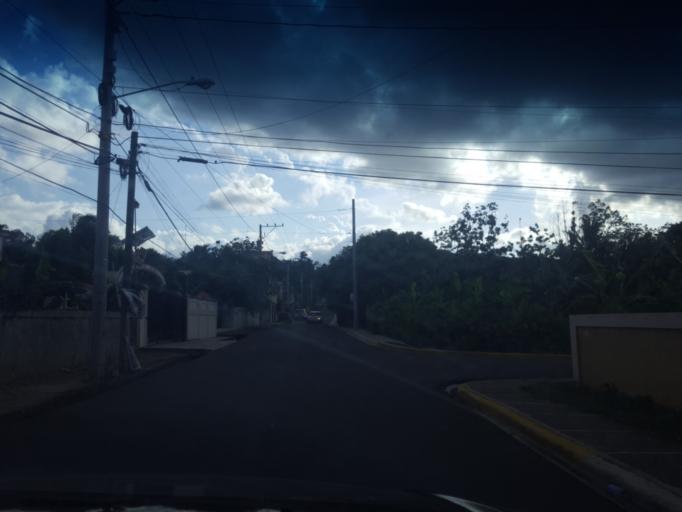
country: DO
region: Santiago
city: Licey al Medio
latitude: 19.3740
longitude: -70.6384
